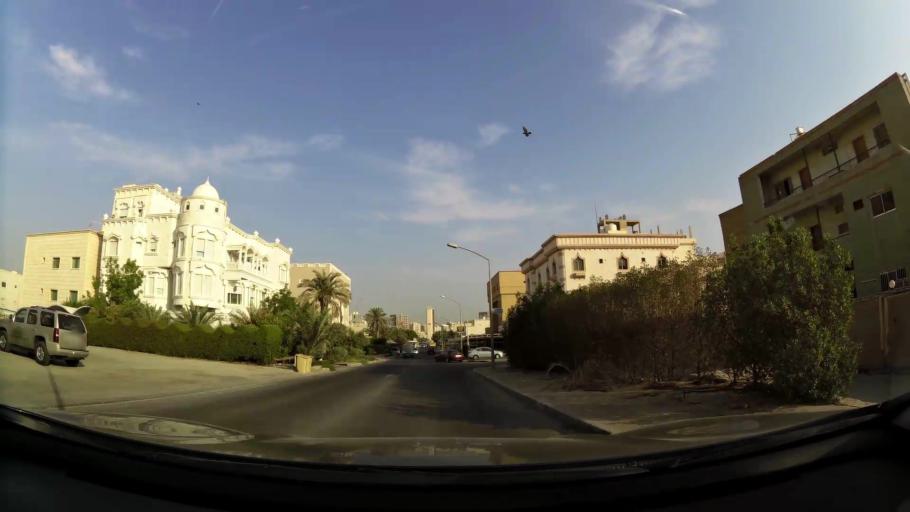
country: KW
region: Muhafazat Hawalli
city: Ar Rumaythiyah
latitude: 29.3187
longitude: 48.0730
